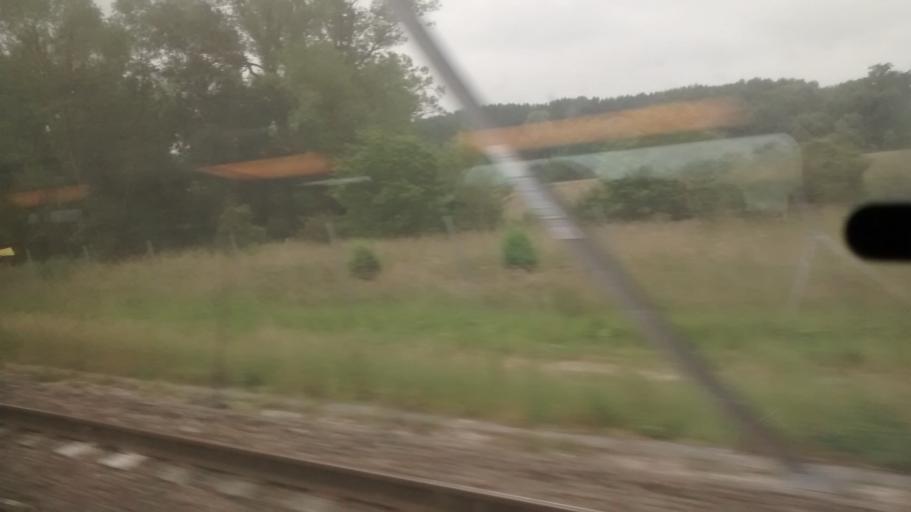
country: FR
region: Ile-de-France
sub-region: Departement de Seine-et-Marne
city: Le Chatelet-en-Brie
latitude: 48.5239
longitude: 2.8161
